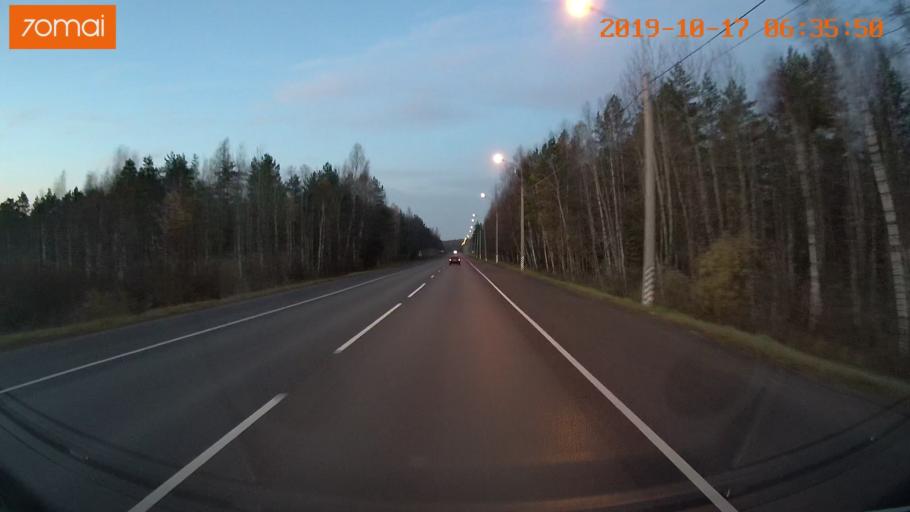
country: RU
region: Ivanovo
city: Novoye Leushino
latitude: 56.6883
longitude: 40.6153
